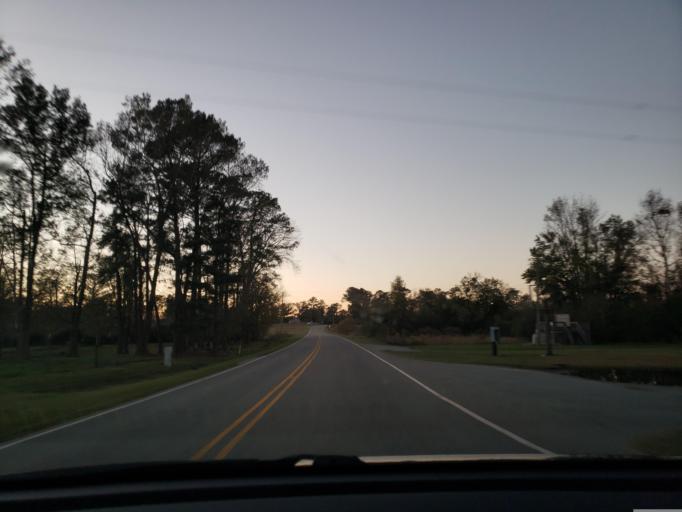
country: US
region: North Carolina
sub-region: Duplin County
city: Beulaville
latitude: 34.8023
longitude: -77.7823
